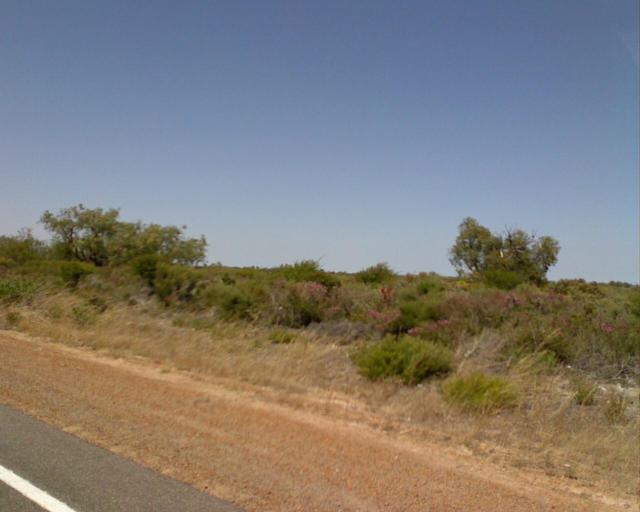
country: AU
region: Western Australia
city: Port Denison
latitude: -29.6568
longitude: 115.2270
